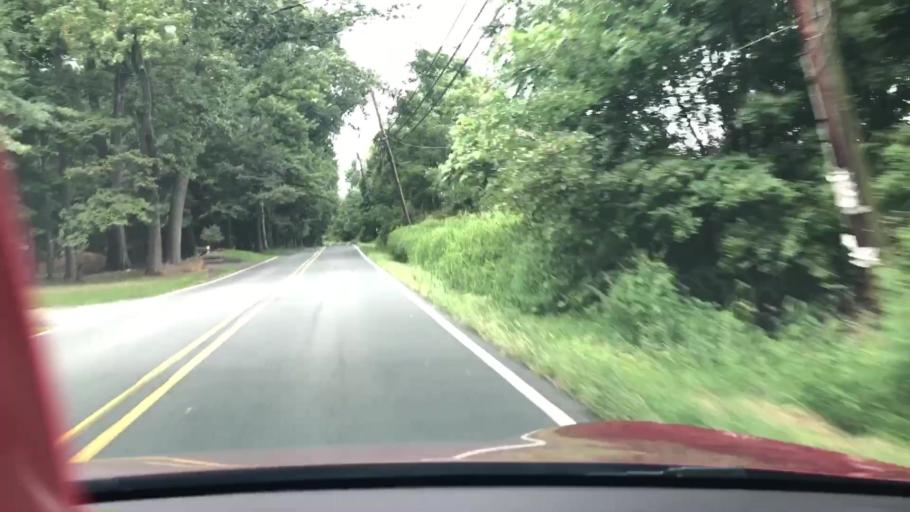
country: US
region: New Jersey
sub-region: Monmouth County
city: Allentown
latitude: 40.1861
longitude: -74.5972
